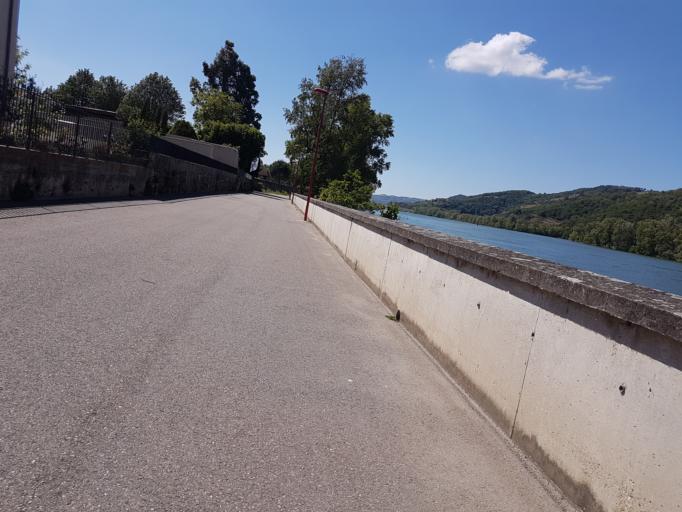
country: FR
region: Rhone-Alpes
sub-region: Departement de la Drome
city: Andancette
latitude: 45.2416
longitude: 4.8028
